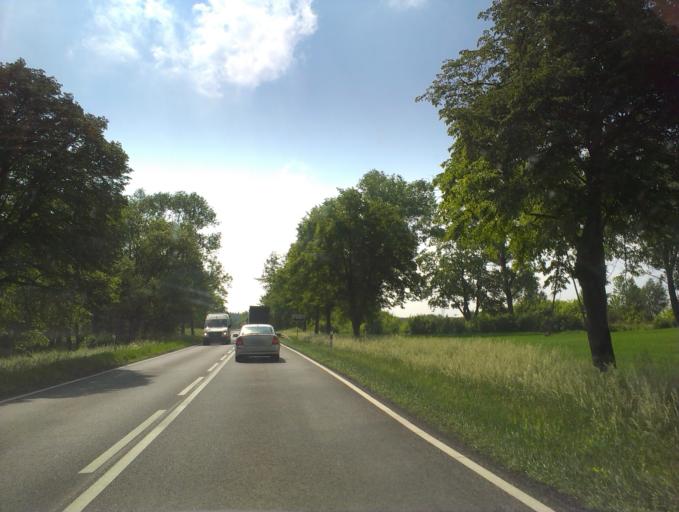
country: PL
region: Greater Poland Voivodeship
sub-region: Powiat zlotowski
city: Okonek
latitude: 53.4793
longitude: 16.8751
